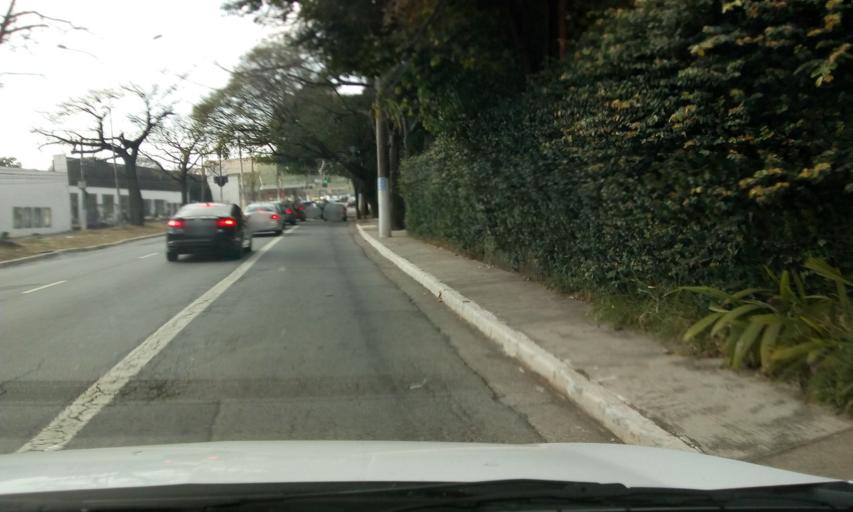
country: BR
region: Sao Paulo
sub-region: Osasco
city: Osasco
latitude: -23.5382
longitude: -46.7266
